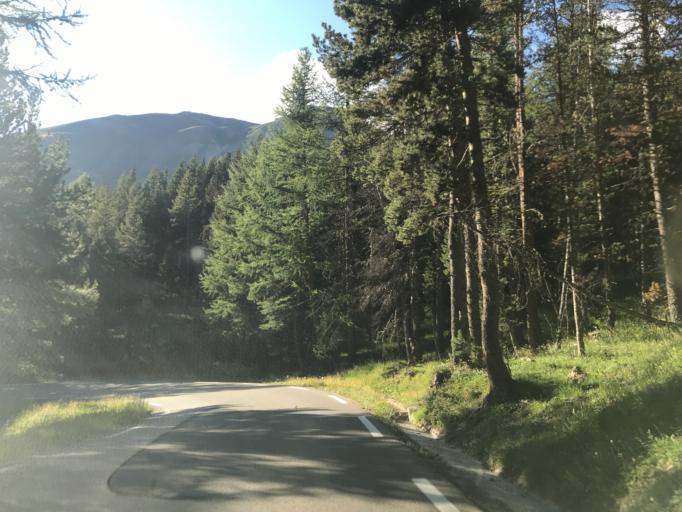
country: FR
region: Provence-Alpes-Cote d'Azur
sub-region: Departement des Hautes-Alpes
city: Villar-Saint-Pancrace
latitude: 44.8054
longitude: 6.7355
